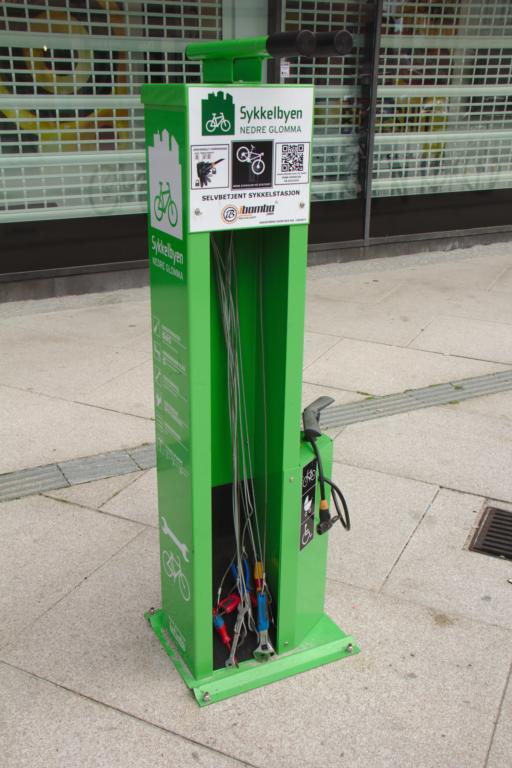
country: NO
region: Ostfold
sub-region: Fredrikstad
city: Fredrikstad
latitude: 59.2131
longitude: 10.9369
